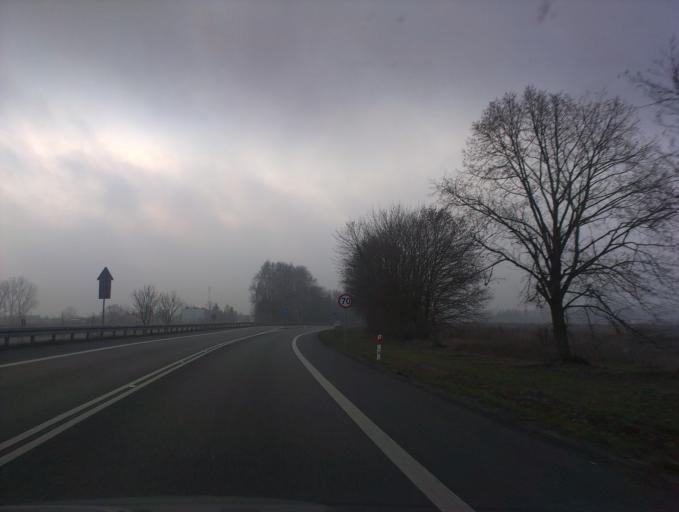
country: PL
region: Greater Poland Voivodeship
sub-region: Powiat chodzieski
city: Chodziez
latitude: 52.9572
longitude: 16.9387
